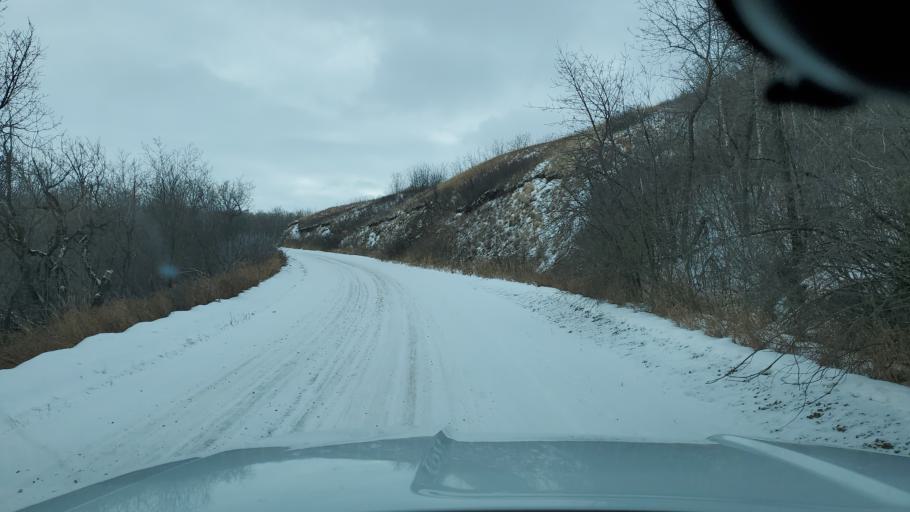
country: CA
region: Saskatchewan
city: White City
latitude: 50.7709
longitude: -104.1492
